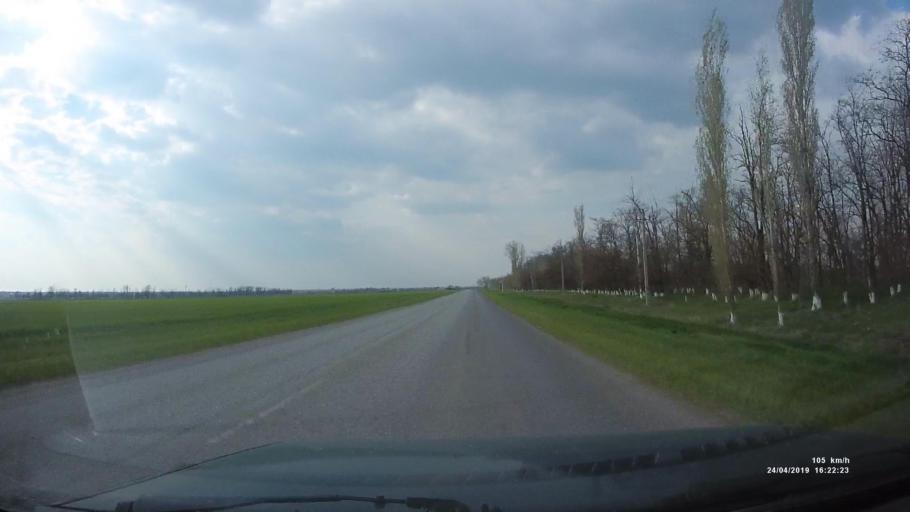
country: RU
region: Rostov
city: Orlovskiy
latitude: 46.8191
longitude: 42.0569
